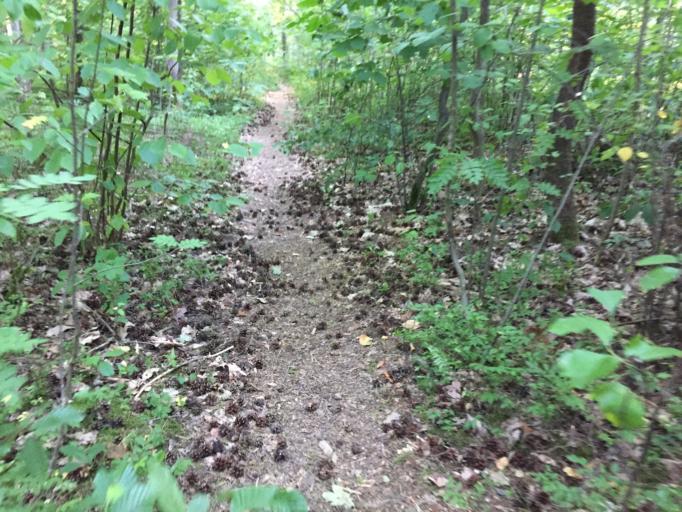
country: DE
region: Bavaria
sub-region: Regierungsbezirk Mittelfranken
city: Erlangen
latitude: 49.5716
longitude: 11.0210
